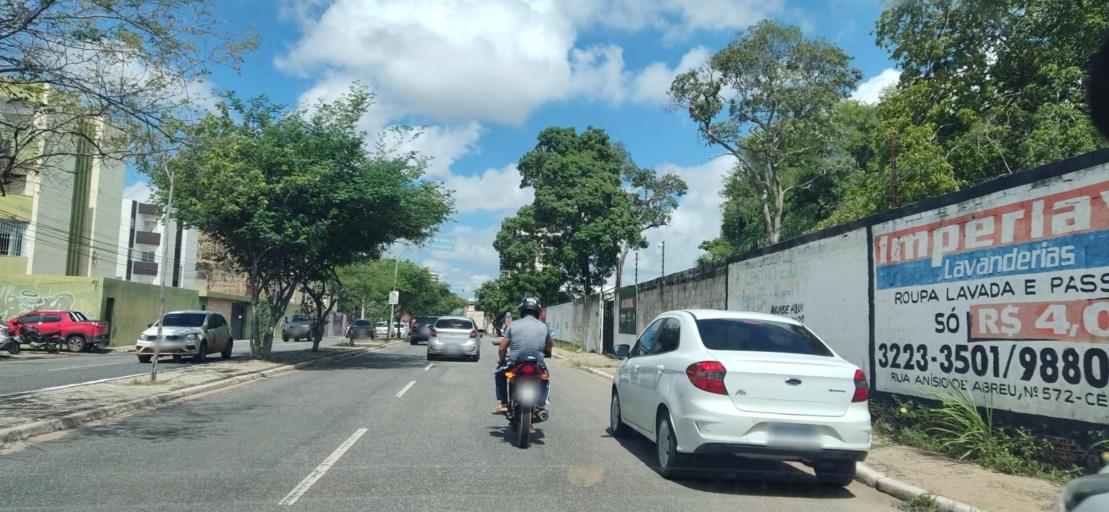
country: BR
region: Piaui
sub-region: Teresina
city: Teresina
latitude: -5.0706
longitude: -42.7702
